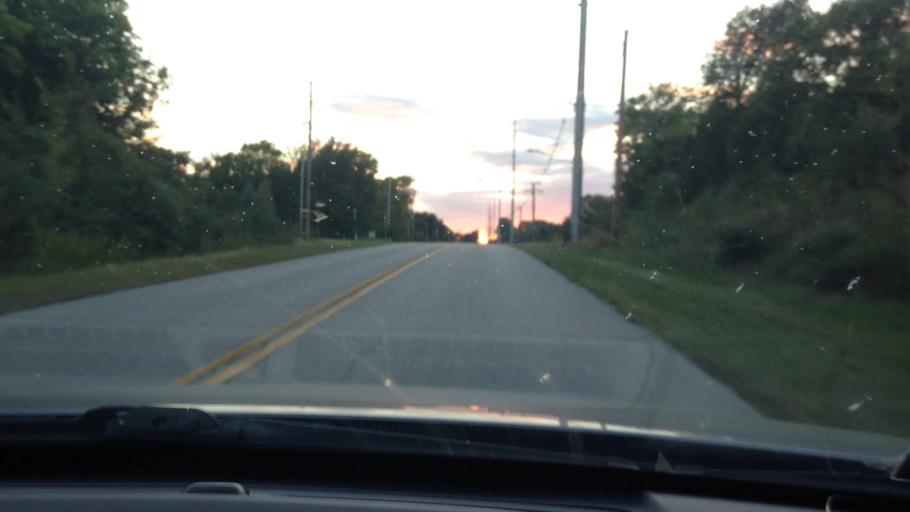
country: US
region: Kansas
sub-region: Leavenworth County
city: Lansing
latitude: 39.1867
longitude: -94.8146
